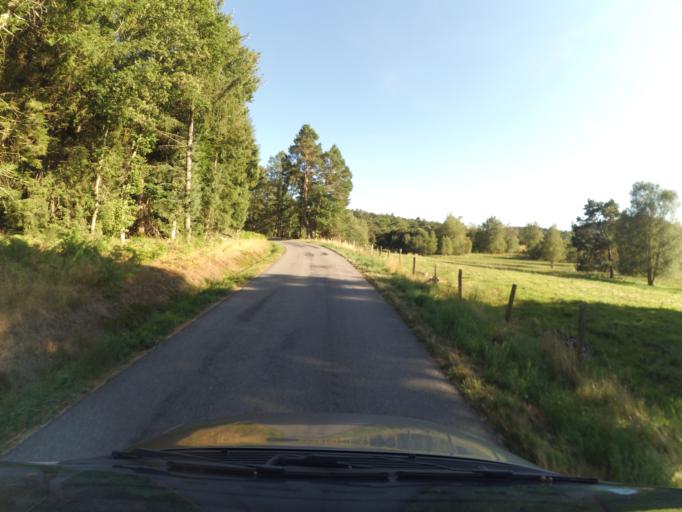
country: FR
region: Limousin
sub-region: Departement de la Creuse
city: Banize
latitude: 45.7186
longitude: 2.0434
